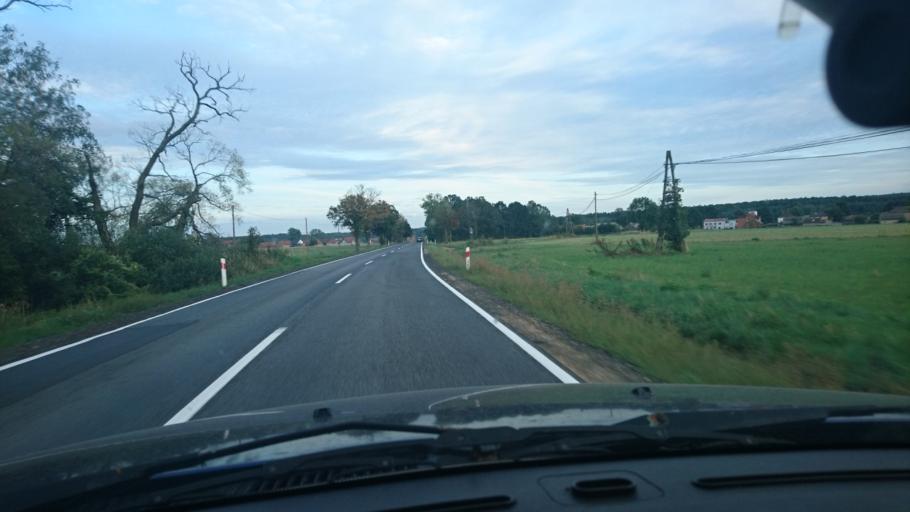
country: PL
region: Silesian Voivodeship
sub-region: Powiat lubliniecki
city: Sierakow Slaski
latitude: 50.8296
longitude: 18.5235
